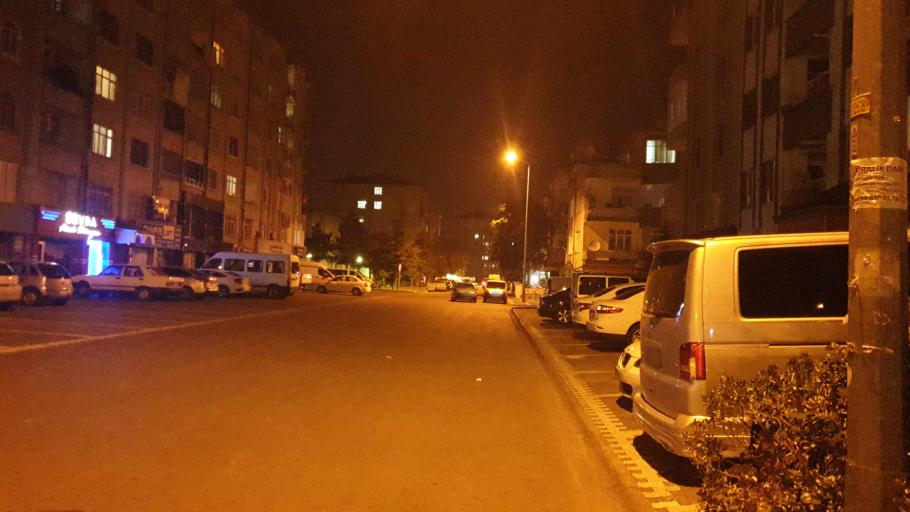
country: TR
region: Kayseri
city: Kayseri
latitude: 38.7298
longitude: 35.4943
